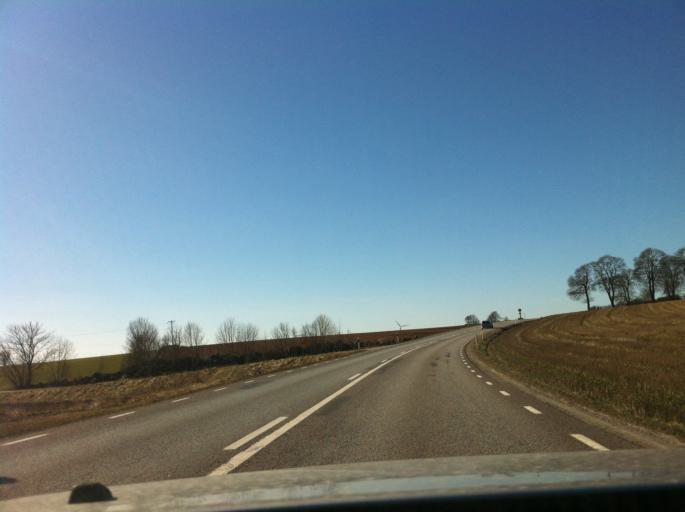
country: SE
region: Vaestra Goetaland
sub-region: Falkopings Kommun
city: Akarp
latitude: 58.0846
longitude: 13.7571
